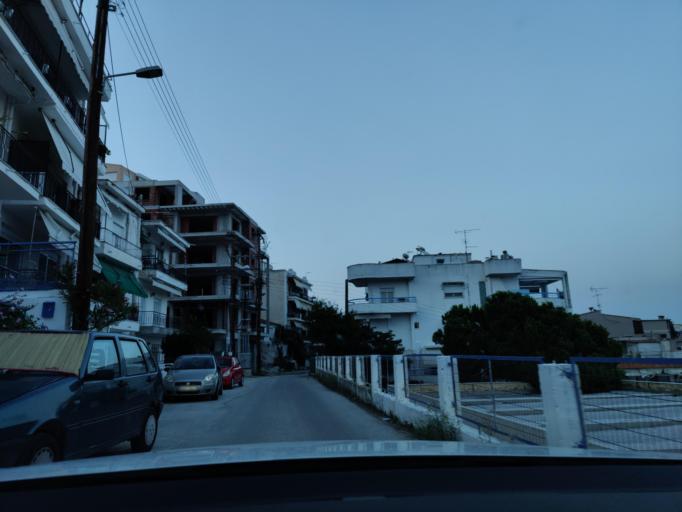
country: GR
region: East Macedonia and Thrace
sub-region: Nomos Kavalas
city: Kavala
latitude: 40.9260
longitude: 24.3856
